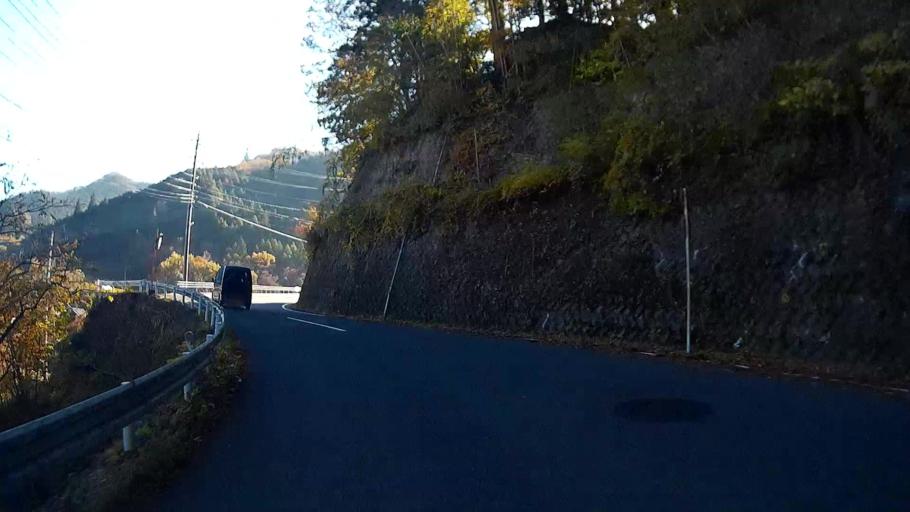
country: JP
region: Yamanashi
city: Uenohara
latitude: 35.5705
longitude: 139.0906
